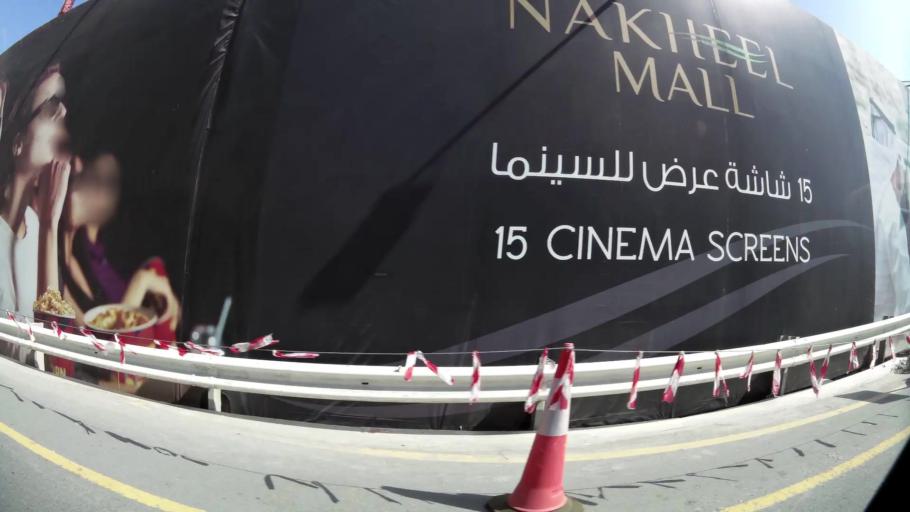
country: AE
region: Dubai
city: Dubai
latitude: 25.1156
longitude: 55.1378
